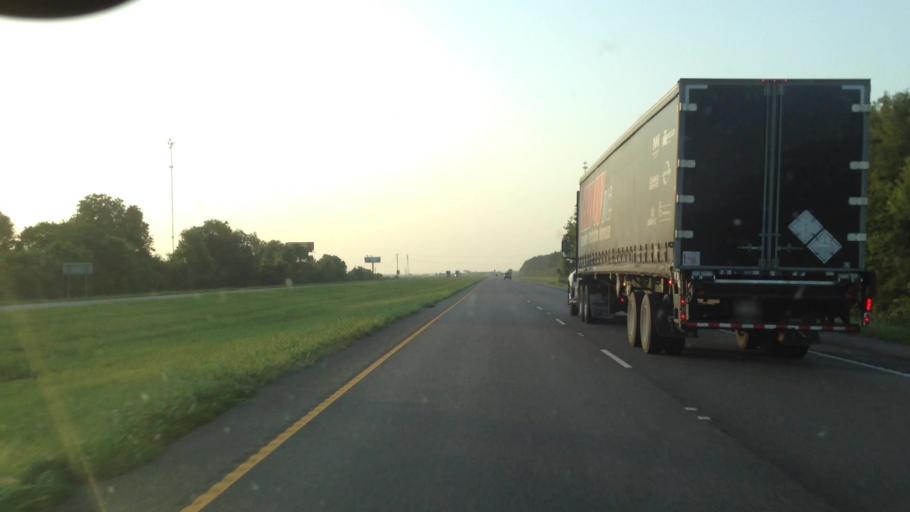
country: US
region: Louisiana
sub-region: Red River Parish
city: Coushatta
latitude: 31.8459
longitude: -93.2934
